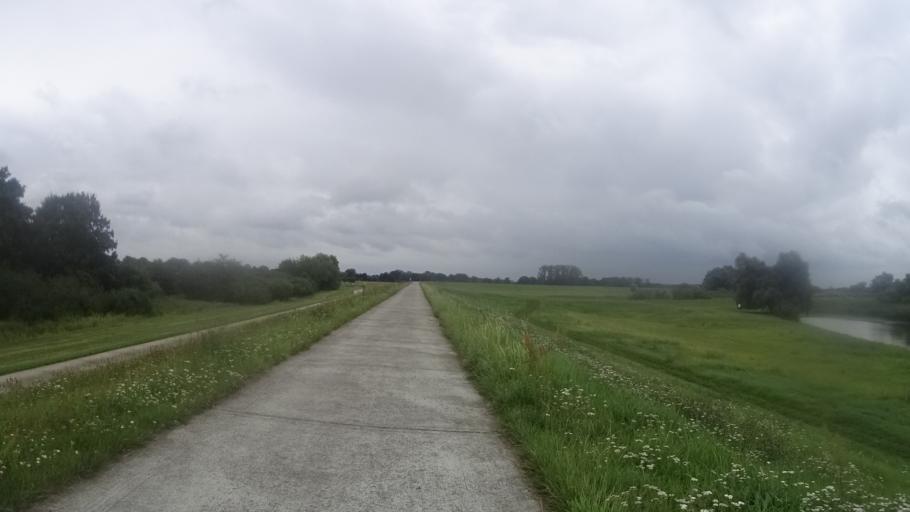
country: DE
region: Lower Saxony
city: Bleckede
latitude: 53.2972
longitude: 10.7747
